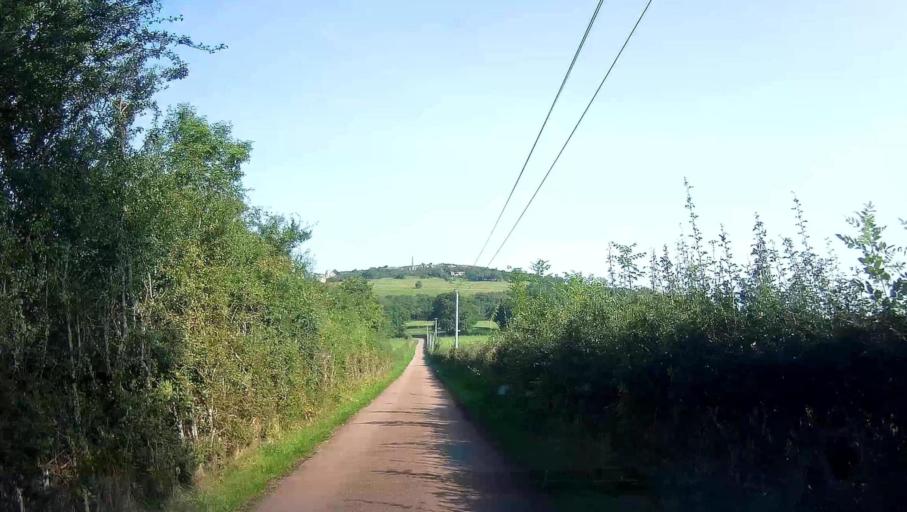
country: FR
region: Bourgogne
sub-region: Departement de Saone-et-Loire
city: Saint-Leger-sur-Dheune
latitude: 46.8944
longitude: 4.6150
